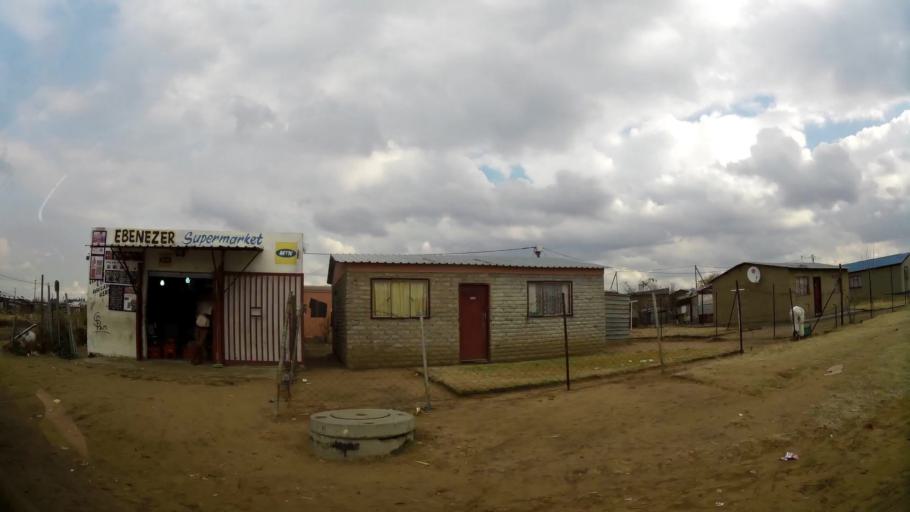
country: ZA
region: Orange Free State
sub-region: Fezile Dabi District Municipality
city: Sasolburg
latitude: -26.8636
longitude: 27.8947
